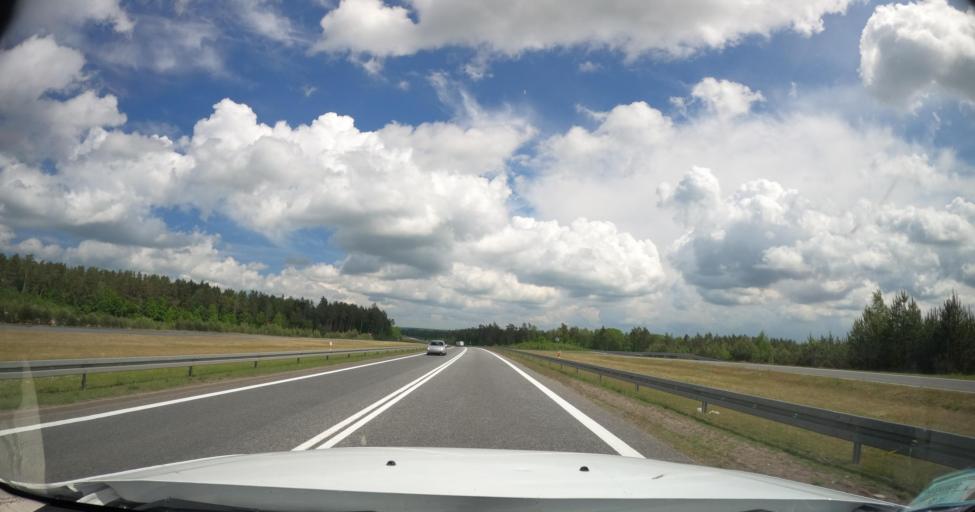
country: PL
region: Pomeranian Voivodeship
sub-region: Slupsk
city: Slupsk
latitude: 54.4320
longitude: 17.0576
